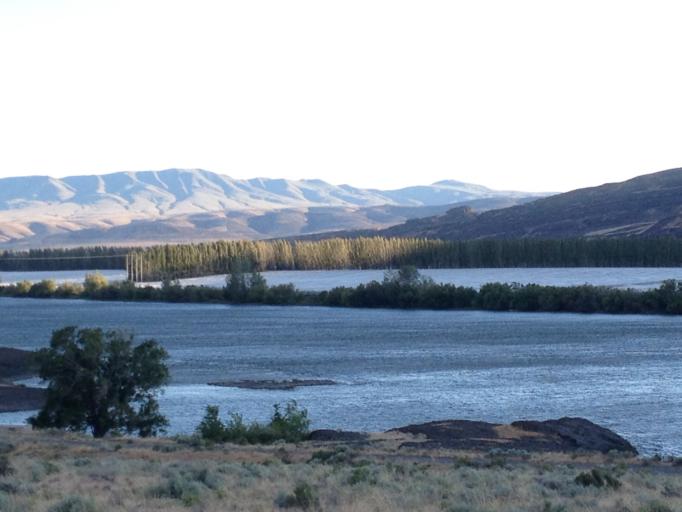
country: US
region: Washington
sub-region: Grant County
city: Mattawa
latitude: 46.8087
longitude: -119.9211
